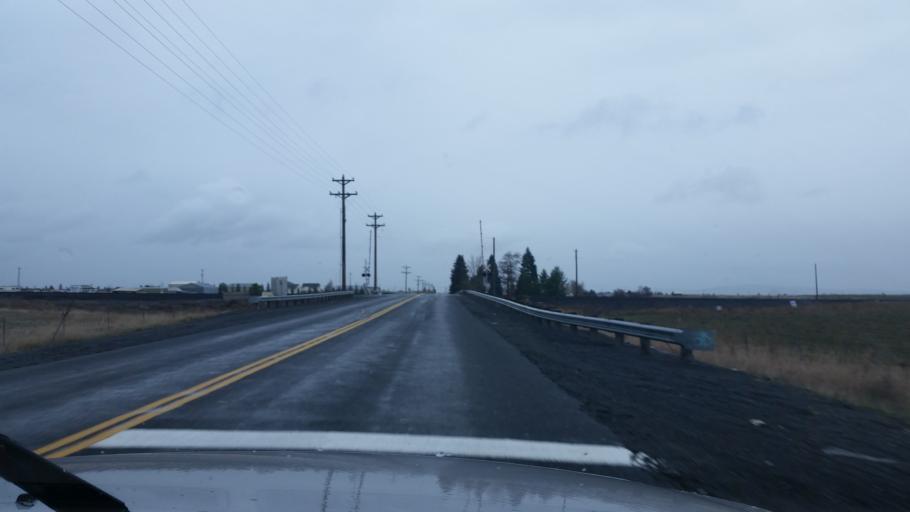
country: US
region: Washington
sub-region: Spokane County
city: Airway Heights
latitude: 47.6617
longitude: -117.6038
